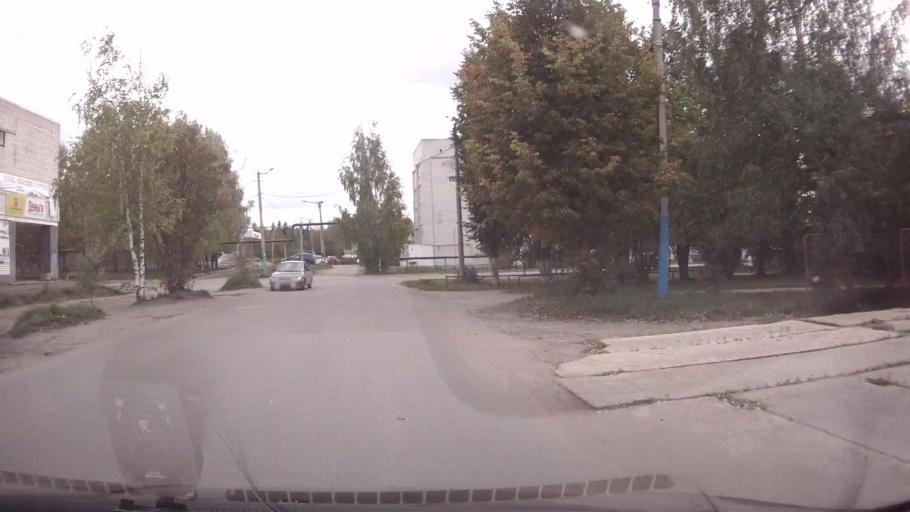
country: RU
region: Mariy-El
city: Kuzhener
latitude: 57.0015
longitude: 48.7402
